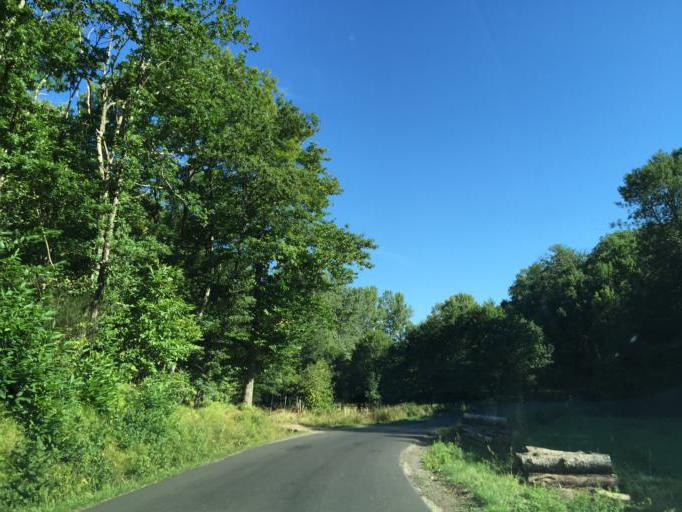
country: FR
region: Midi-Pyrenees
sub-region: Departement de l'Aveyron
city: Laissac
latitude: 44.3704
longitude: 2.7976
